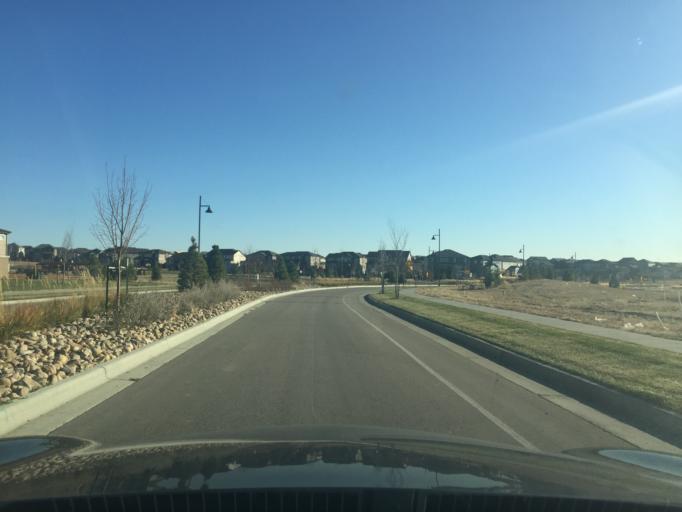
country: US
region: Colorado
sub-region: Boulder County
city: Erie
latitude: 40.0485
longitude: -105.0360
